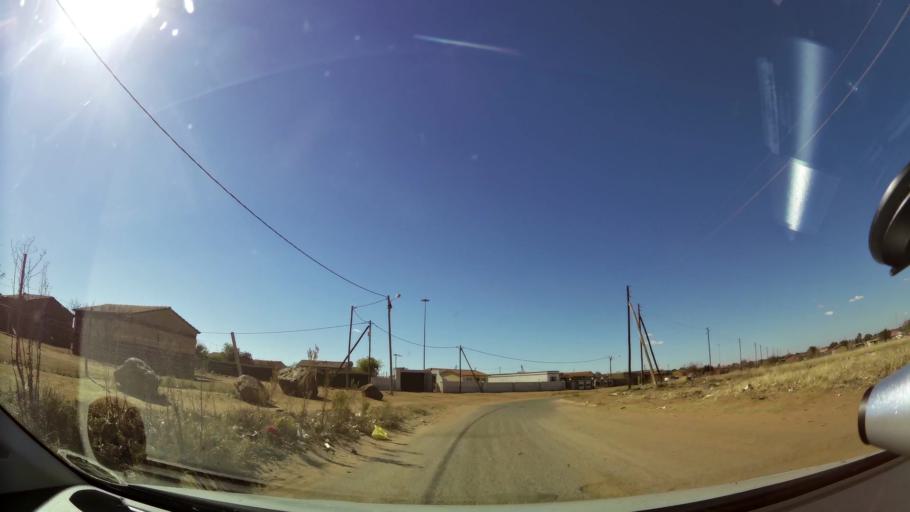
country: ZA
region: North-West
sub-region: Dr Kenneth Kaunda District Municipality
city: Klerksdorp
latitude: -26.8682
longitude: 26.5721
